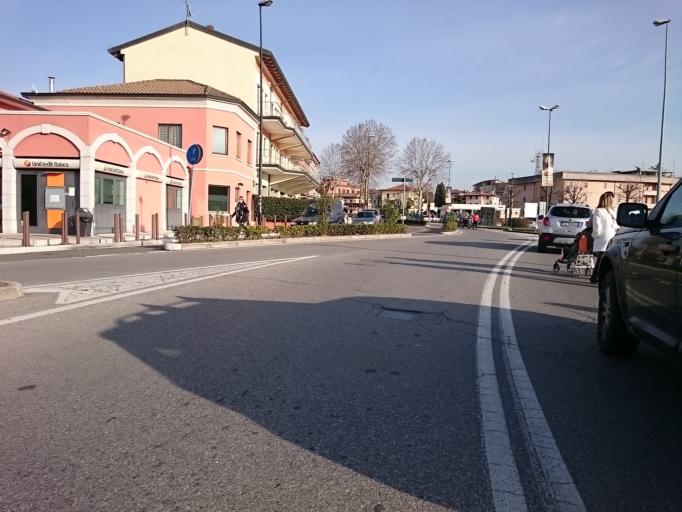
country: IT
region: Veneto
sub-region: Provincia di Verona
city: Peschiera del Garda
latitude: 45.4407
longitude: 10.6984
